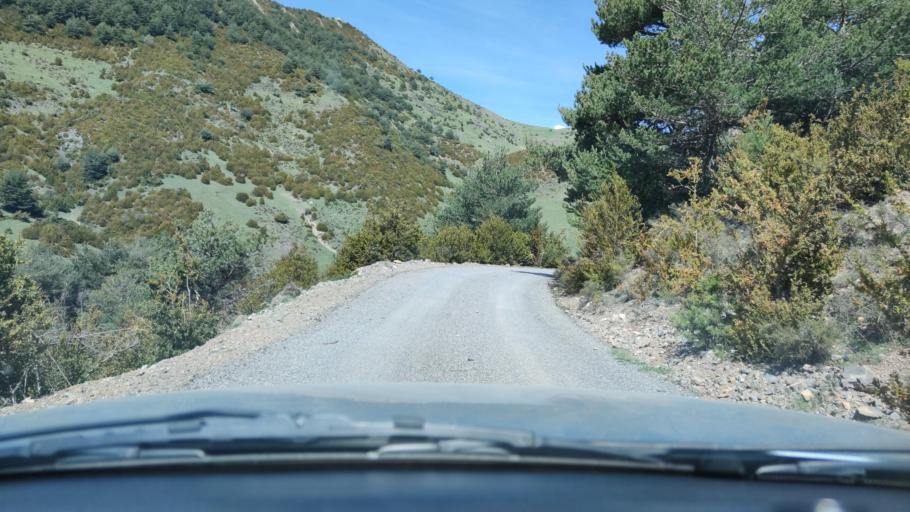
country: ES
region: Catalonia
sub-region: Provincia de Lleida
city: Sort
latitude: 42.3114
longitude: 1.1647
